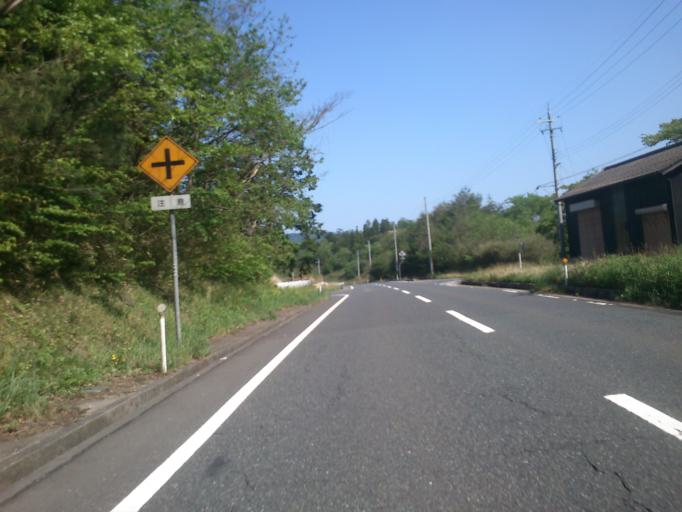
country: JP
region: Kyoto
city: Miyazu
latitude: 35.6645
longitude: 135.1026
